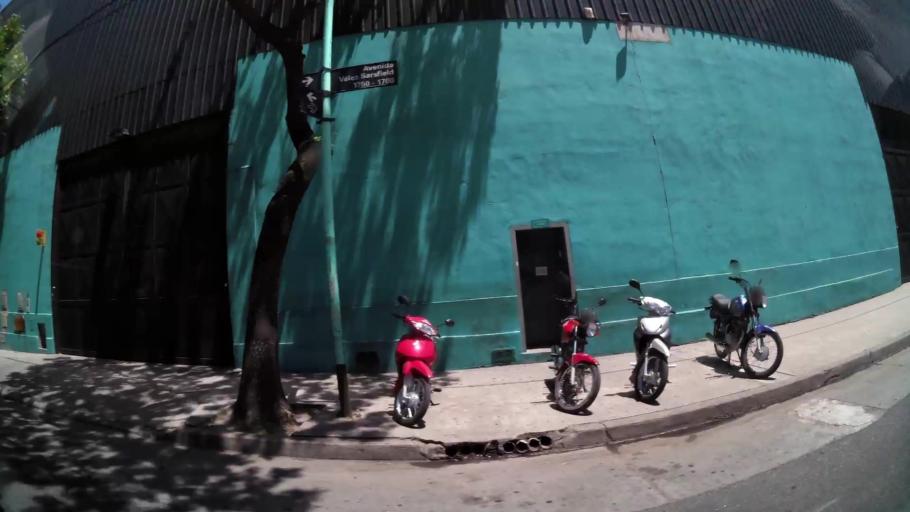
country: AR
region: Buenos Aires
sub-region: Partido de Avellaneda
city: Avellaneda
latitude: -34.6561
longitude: -58.3887
